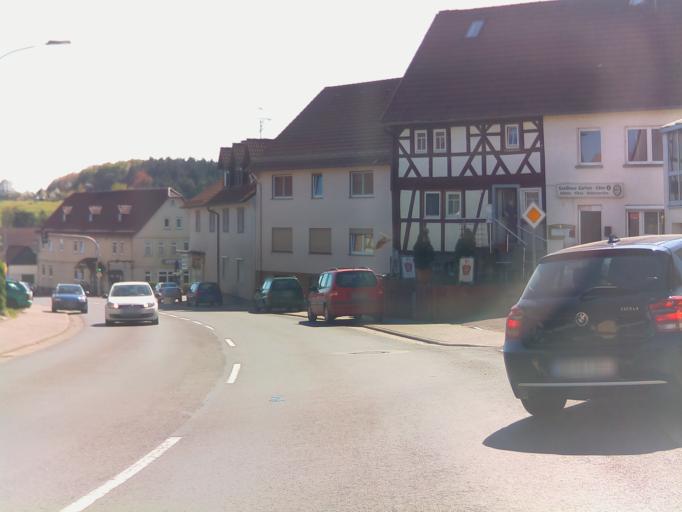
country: DE
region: Hesse
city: Herbstein
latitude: 50.5604
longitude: 9.3470
